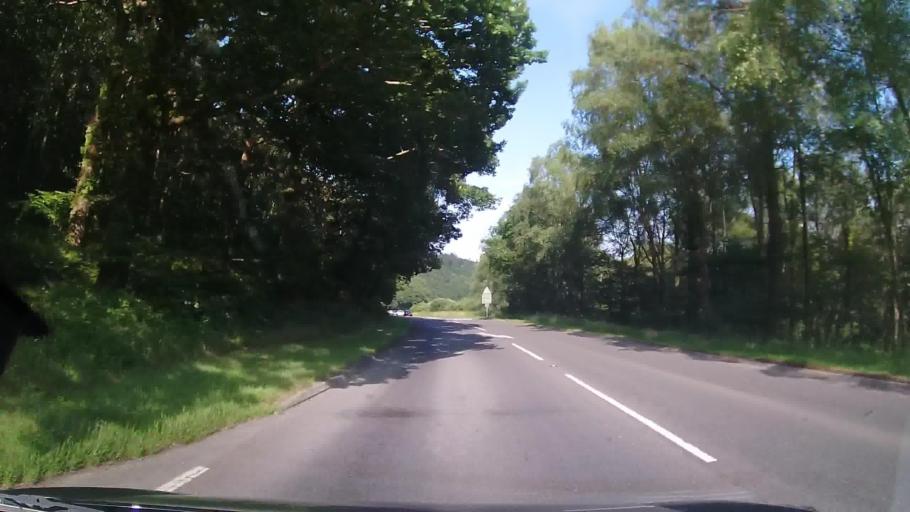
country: GB
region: Wales
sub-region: Gwynedd
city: Penrhyndeudraeth
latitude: 52.9414
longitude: -4.0385
